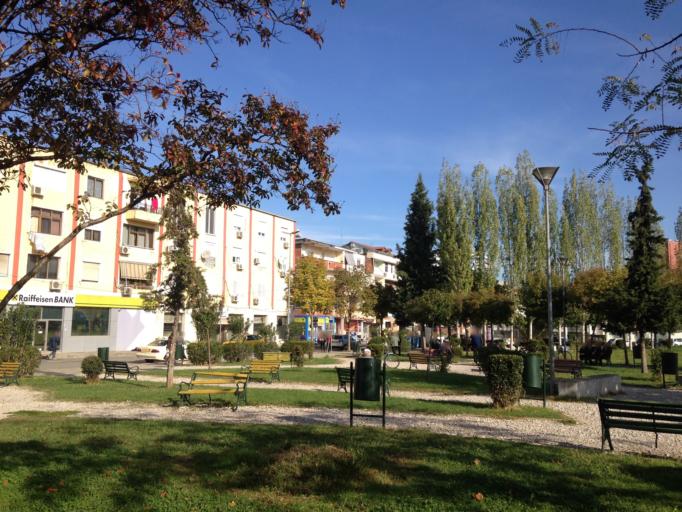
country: AL
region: Tirane
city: Tirana
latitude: 41.3189
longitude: 19.8084
